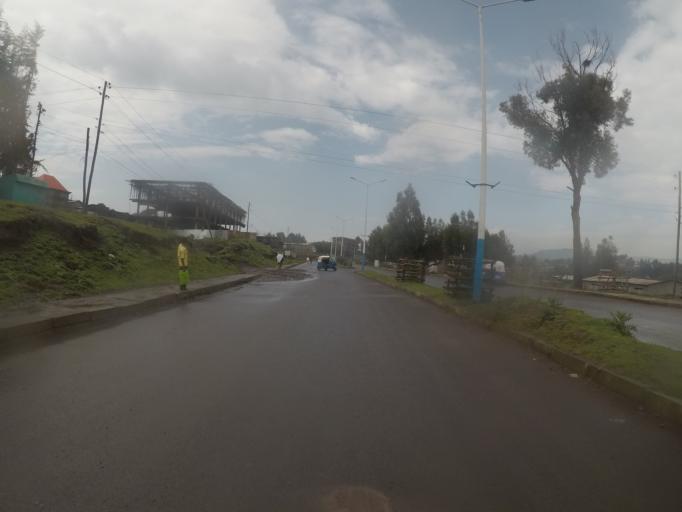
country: ET
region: Amhara
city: Debark'
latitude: 13.1423
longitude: 37.8937
